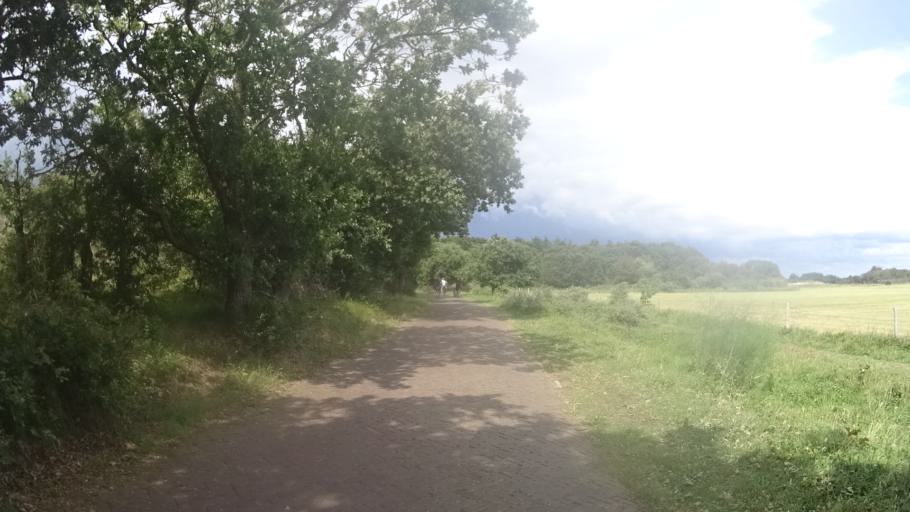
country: NL
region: North Holland
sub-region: Gemeente Bergen
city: Egmond aan Zee
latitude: 52.5928
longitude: 4.6370
